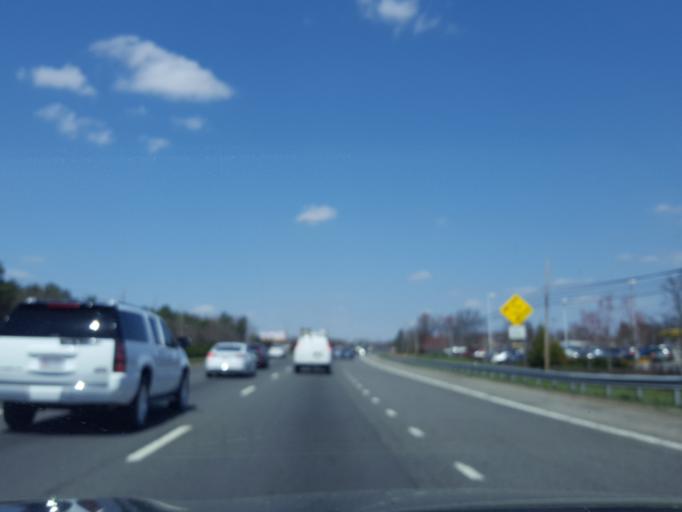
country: US
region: Maryland
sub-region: Prince George's County
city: Brandywine
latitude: 38.6767
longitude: -76.8755
